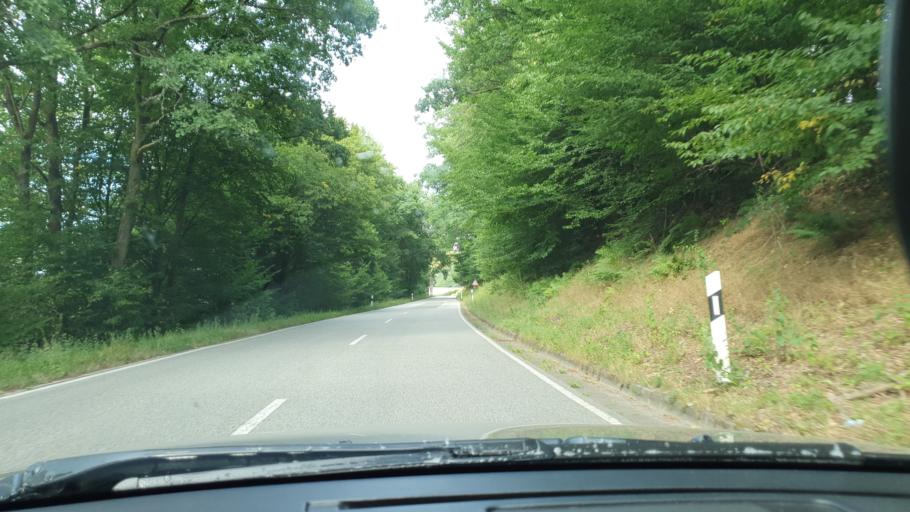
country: DE
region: Rheinland-Pfalz
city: Steinalben
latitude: 49.3202
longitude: 7.6488
